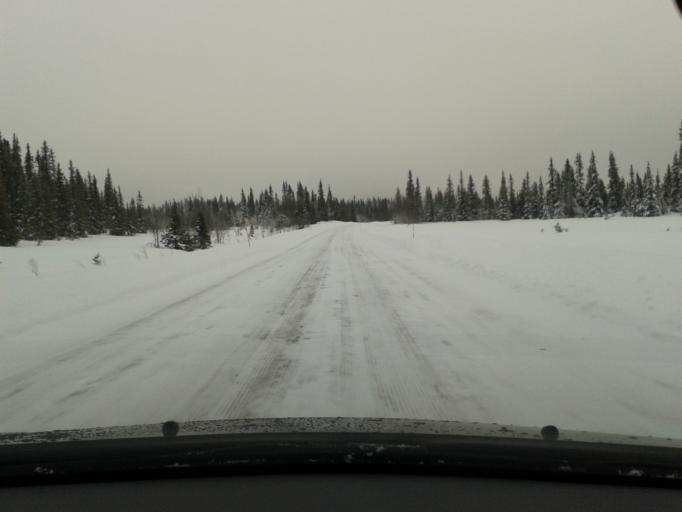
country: SE
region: Vaesterbotten
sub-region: Vilhelmina Kommun
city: Sjoberg
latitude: 65.0795
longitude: 15.8812
